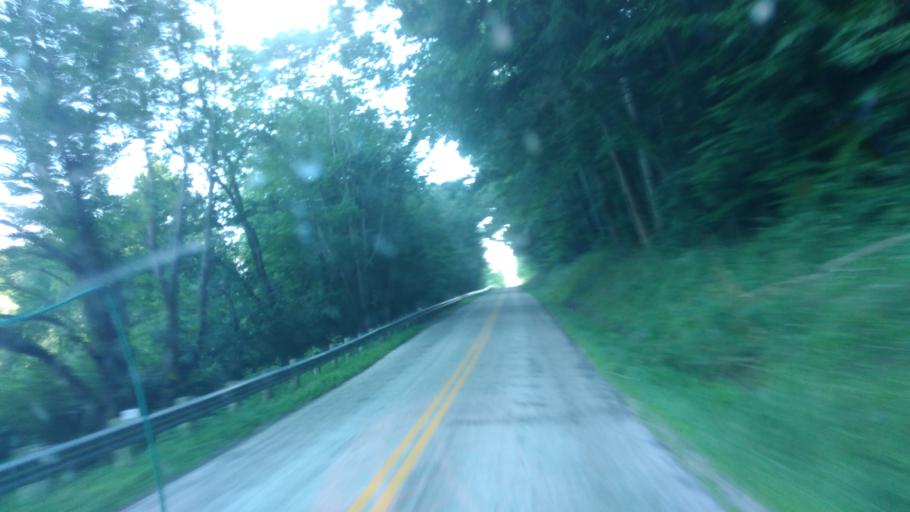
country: US
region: Ohio
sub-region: Ashland County
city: Loudonville
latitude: 40.7240
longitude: -82.1599
